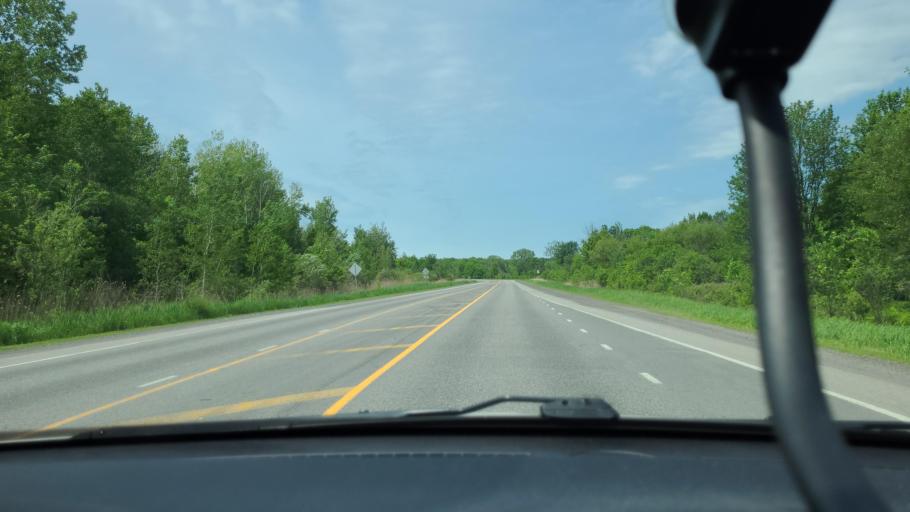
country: CA
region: Quebec
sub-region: Lanaudiere
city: Saint-Jacques
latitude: 45.9715
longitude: -73.5384
